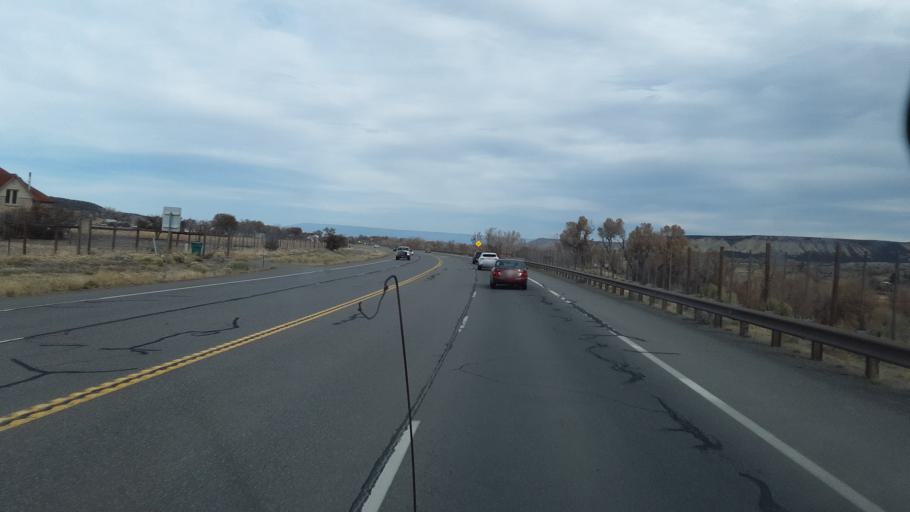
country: US
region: Colorado
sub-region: Montrose County
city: Montrose
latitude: 38.3203
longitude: -107.7755
